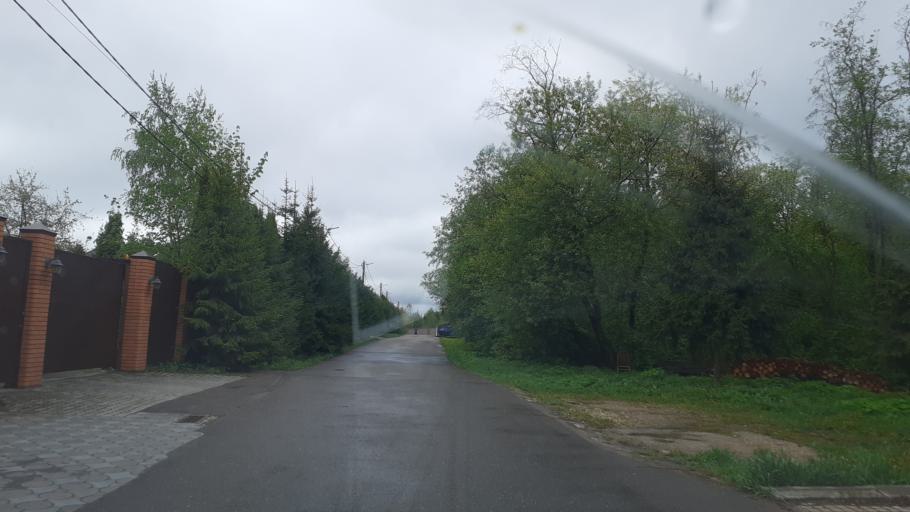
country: RU
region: Moskovskaya
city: Gorki Vtoryye
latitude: 55.7055
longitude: 37.2010
